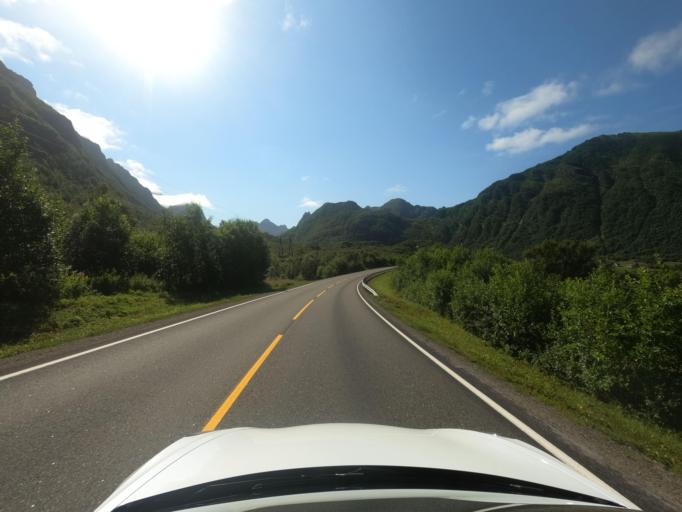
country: NO
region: Nordland
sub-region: Hadsel
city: Stokmarknes
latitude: 68.4504
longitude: 15.0508
